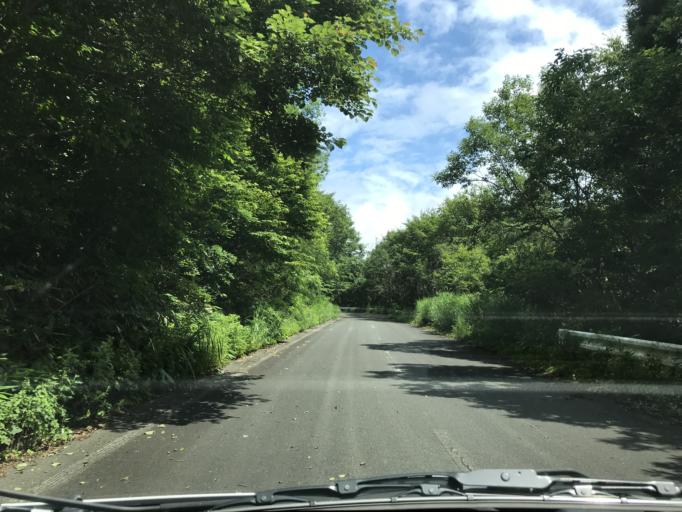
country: JP
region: Iwate
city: Tono
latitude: 39.0976
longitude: 141.4175
